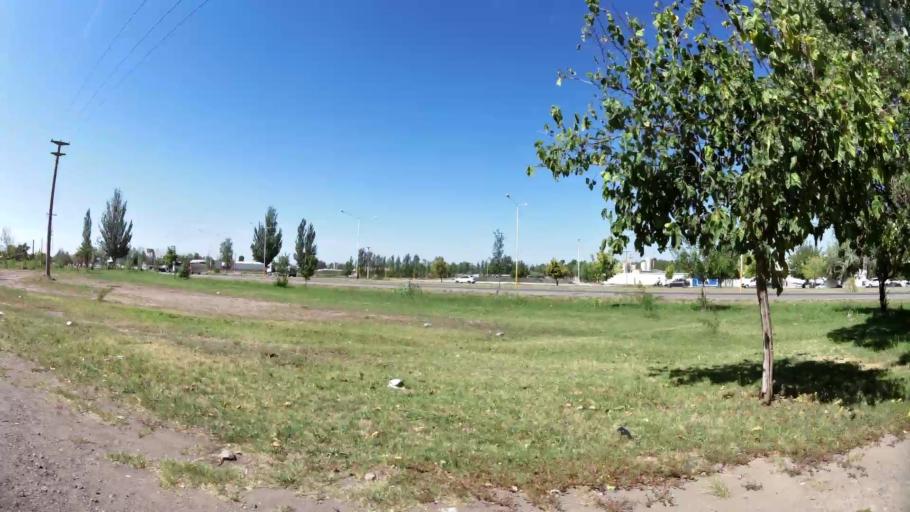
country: AR
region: Mendoza
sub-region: Departamento de Godoy Cruz
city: Godoy Cruz
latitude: -32.9768
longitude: -68.8472
